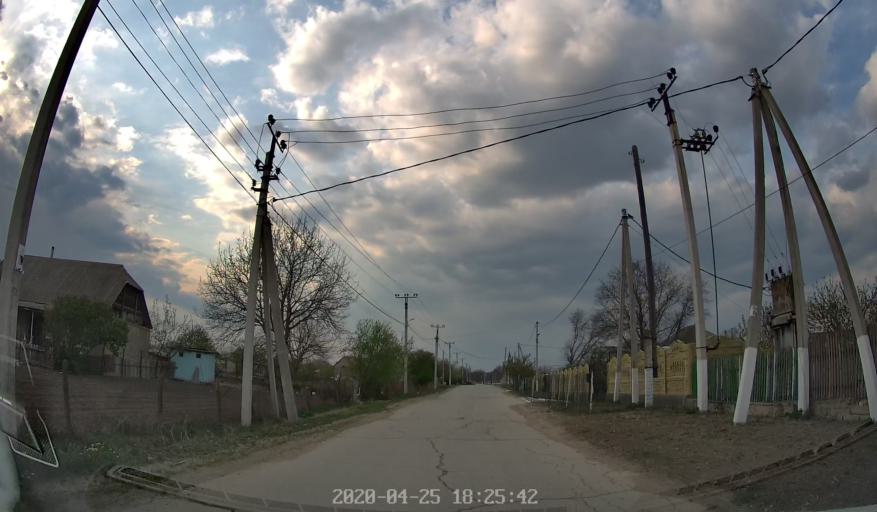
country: MD
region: Criuleni
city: Criuleni
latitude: 47.1628
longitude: 29.1284
